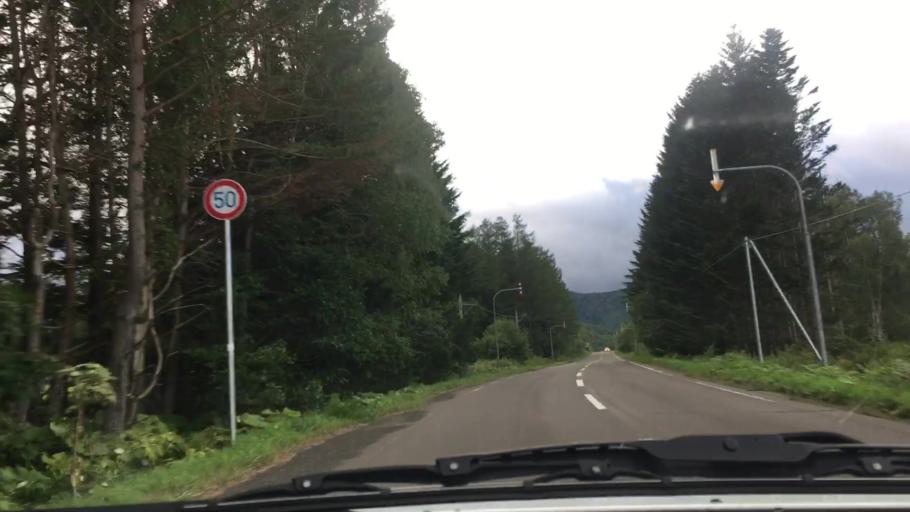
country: JP
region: Hokkaido
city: Shimo-furano
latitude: 43.0507
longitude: 142.6697
